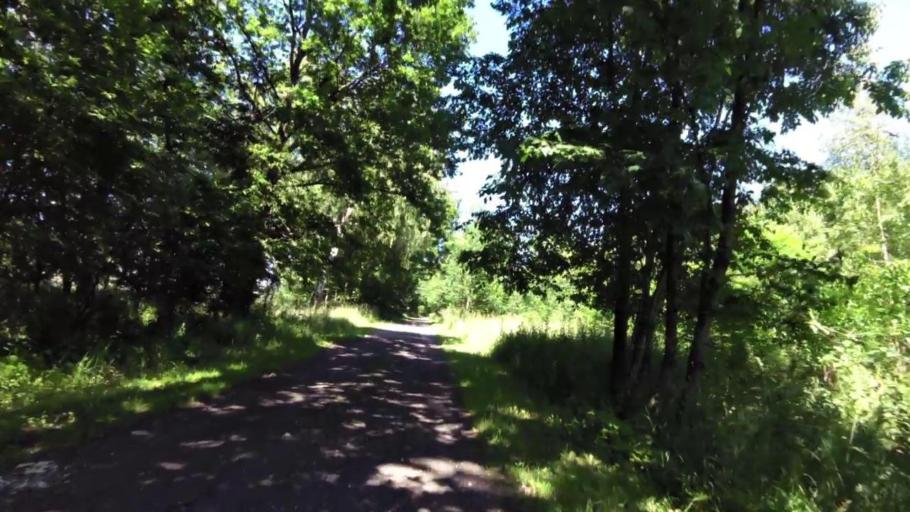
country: PL
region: West Pomeranian Voivodeship
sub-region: Powiat kolobrzeski
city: Goscino
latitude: 54.0420
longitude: 15.7224
